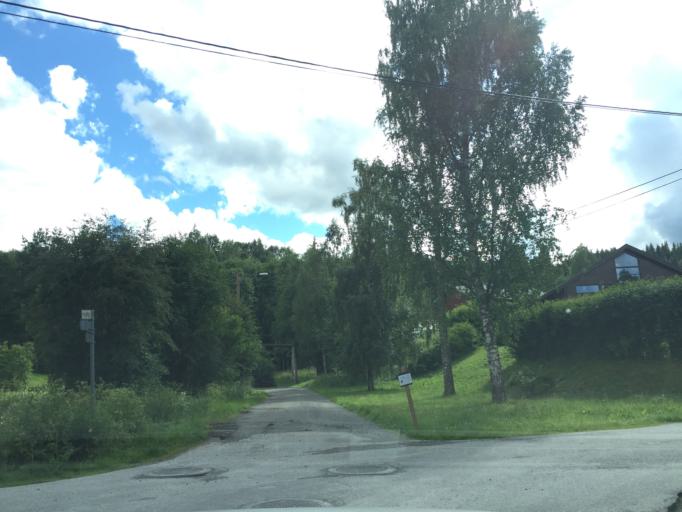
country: NO
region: Hedmark
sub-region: Kongsvinger
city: Kongsvinger
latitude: 60.1836
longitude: 12.0060
